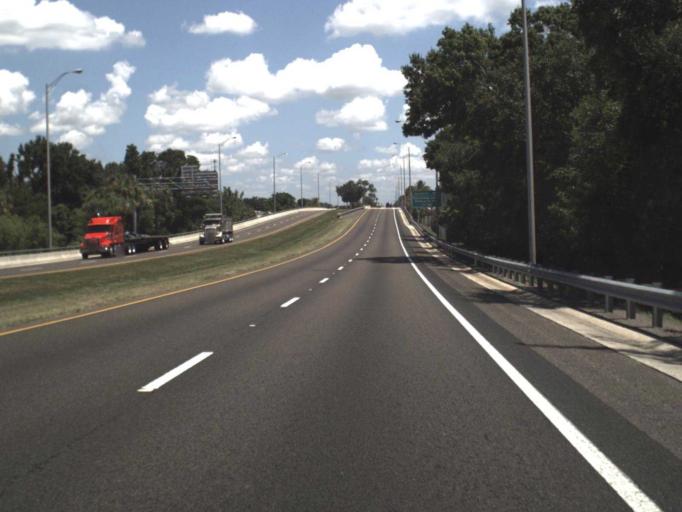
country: US
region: Florida
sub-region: Hillsborough County
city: Tampa
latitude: 27.9296
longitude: -82.4852
